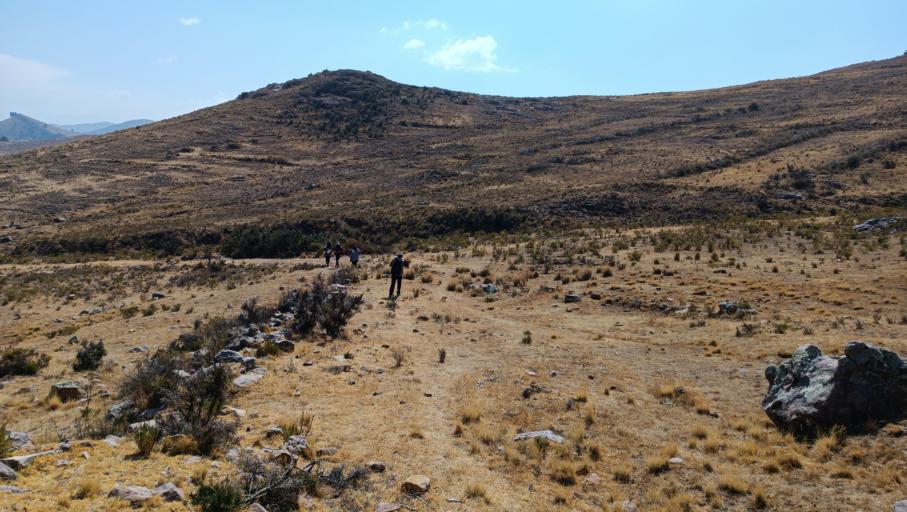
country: BO
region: La Paz
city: Batallas
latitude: -16.3462
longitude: -68.6589
